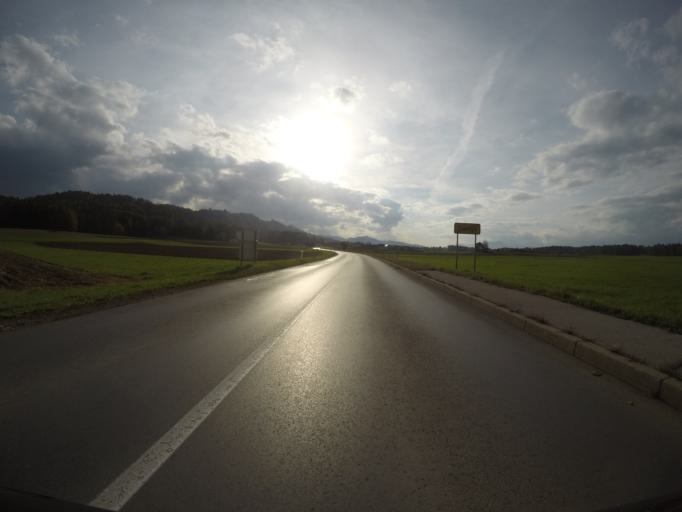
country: SI
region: Vodice
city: Vodice
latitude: 46.1783
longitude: 14.4603
